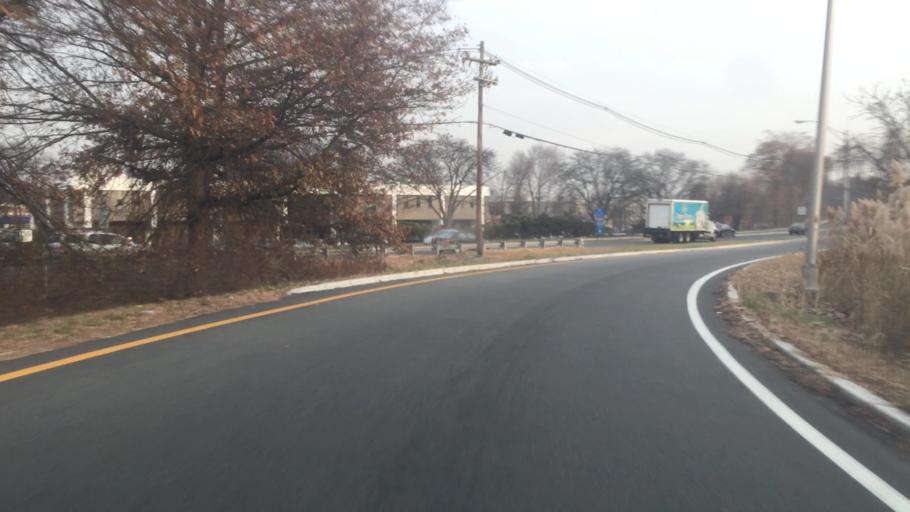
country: US
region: New Jersey
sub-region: Morris County
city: Rockaway
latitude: 40.8927
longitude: -74.4814
